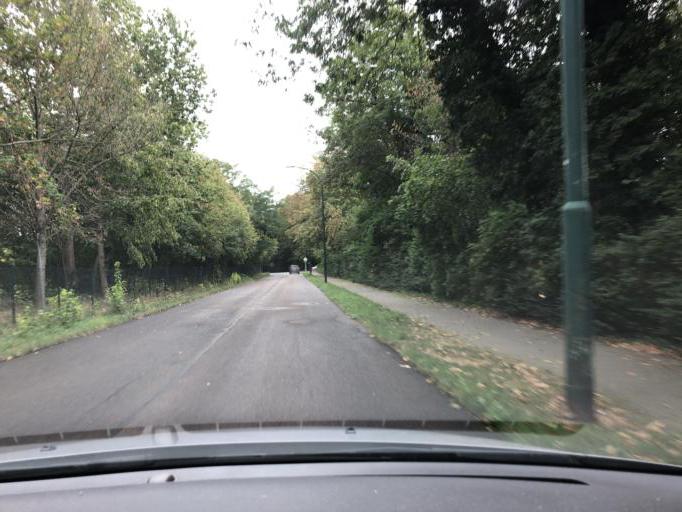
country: DE
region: Saxony-Anhalt
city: Koethen
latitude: 51.7543
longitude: 11.9513
